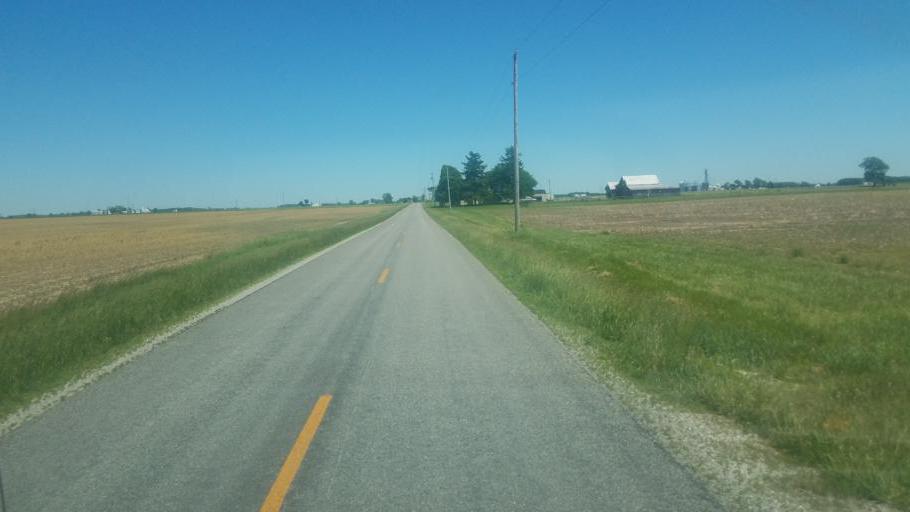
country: US
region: Ohio
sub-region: Shelby County
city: Sidney
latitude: 40.2114
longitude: -84.1198
